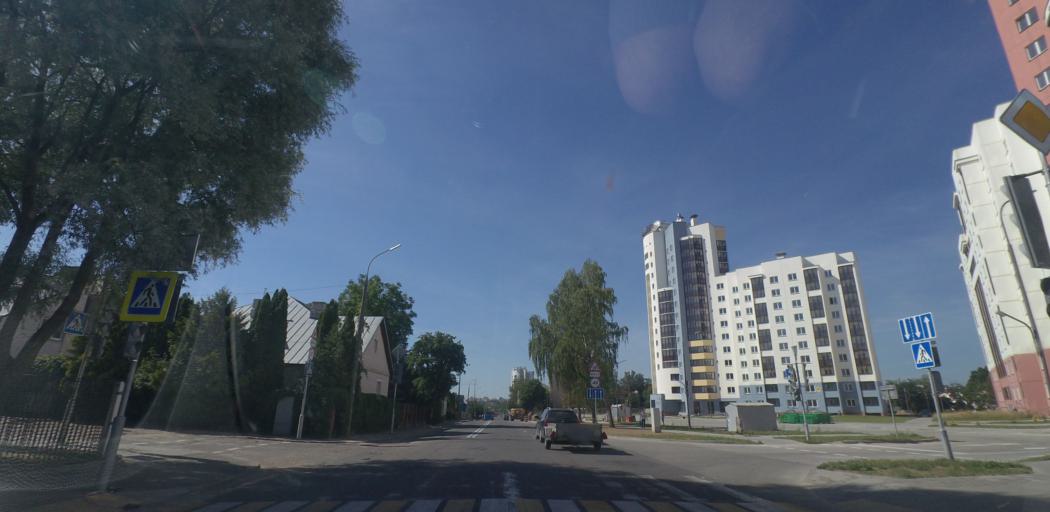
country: BY
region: Grodnenskaya
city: Hrodna
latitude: 53.6778
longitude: 23.8542
